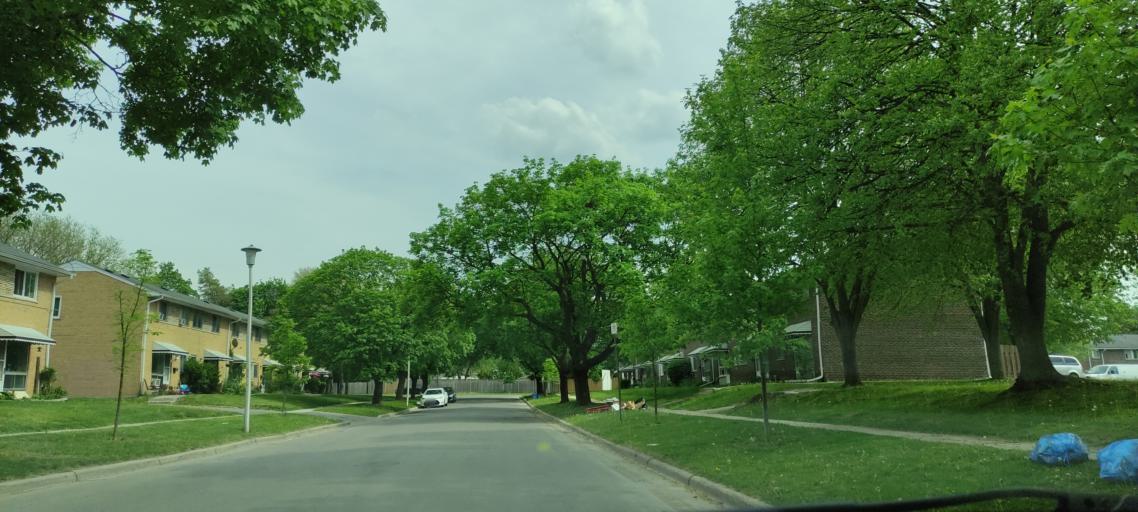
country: CA
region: Ontario
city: London
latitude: 43.0211
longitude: -81.2378
